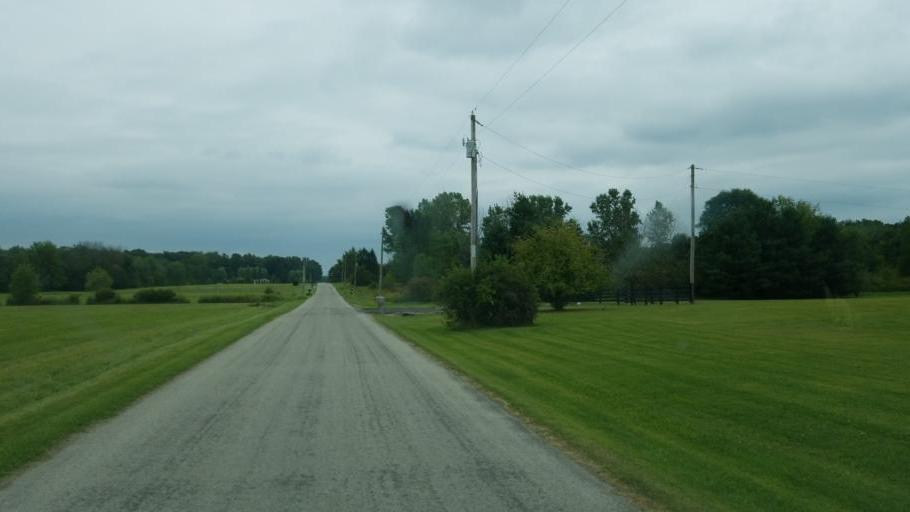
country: US
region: Ohio
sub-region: Morrow County
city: Mount Gilead
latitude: 40.5279
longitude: -82.8020
